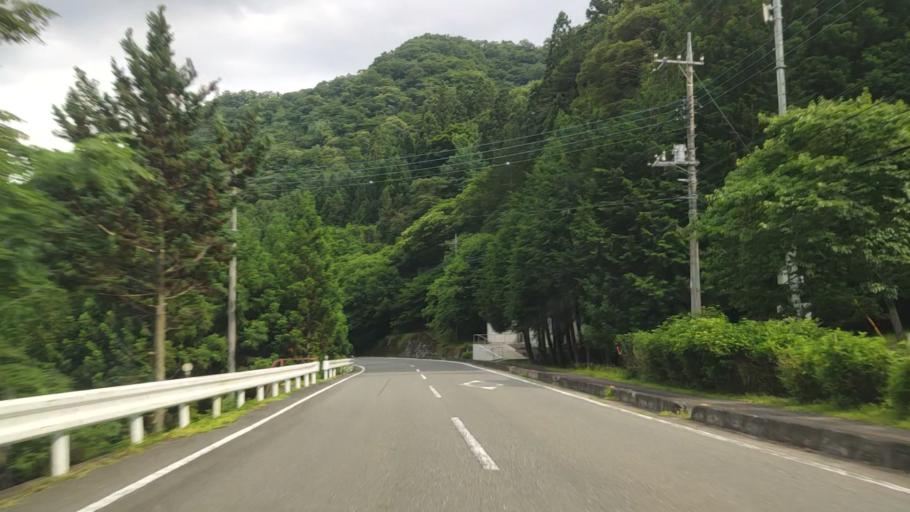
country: JP
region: Gunma
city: Tomioka
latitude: 36.0542
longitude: 138.8611
